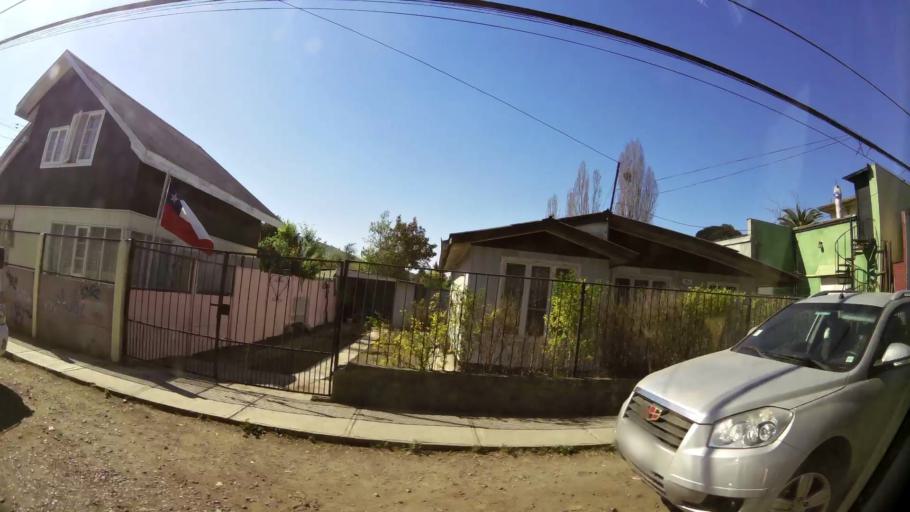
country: CL
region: Santiago Metropolitan
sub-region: Provincia de Talagante
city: Penaflor
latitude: -33.6070
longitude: -70.9031
